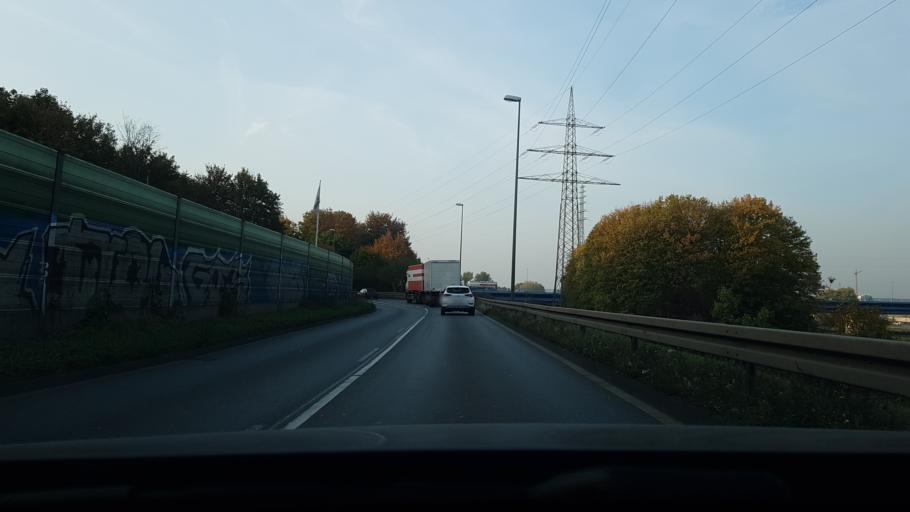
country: DE
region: North Rhine-Westphalia
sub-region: Regierungsbezirk Dusseldorf
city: Hochfeld
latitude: 51.4101
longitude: 6.7336
